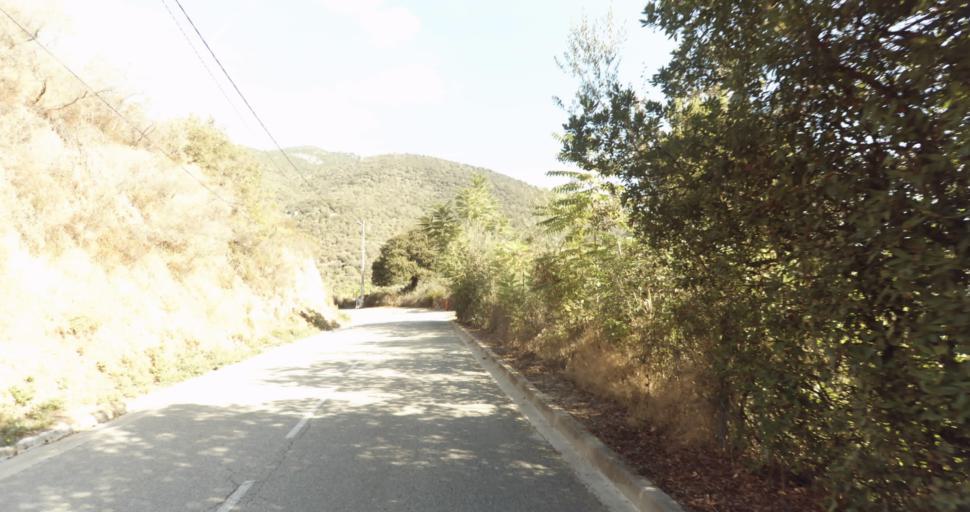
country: FR
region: Corsica
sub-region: Departement de la Corse-du-Sud
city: Ajaccio
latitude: 41.9275
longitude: 8.7066
